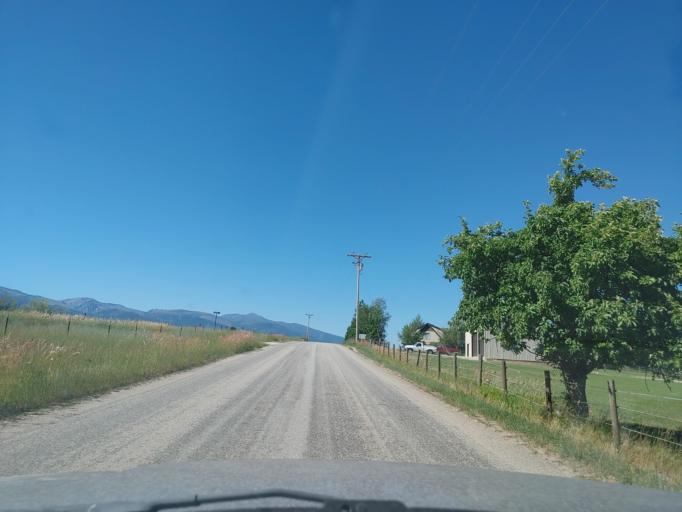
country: US
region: Montana
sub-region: Ravalli County
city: Hamilton
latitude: 46.3150
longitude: -114.2076
